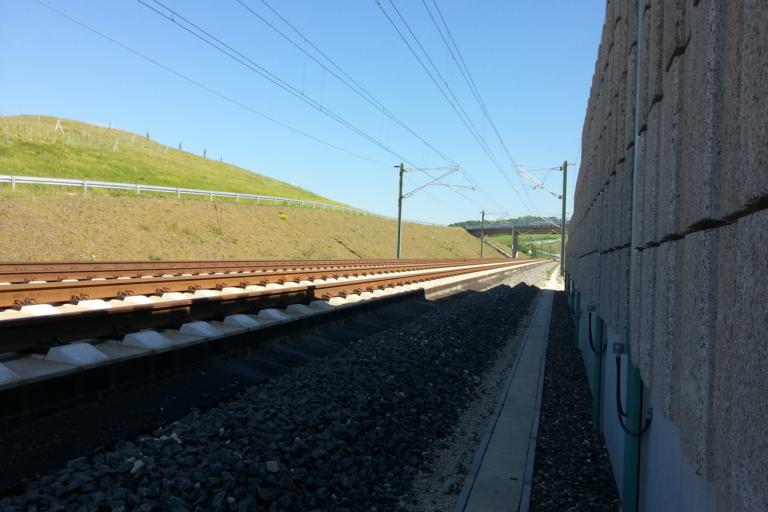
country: DE
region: Bavaria
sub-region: Upper Franconia
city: Rodental
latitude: 50.3065
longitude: 11.0072
